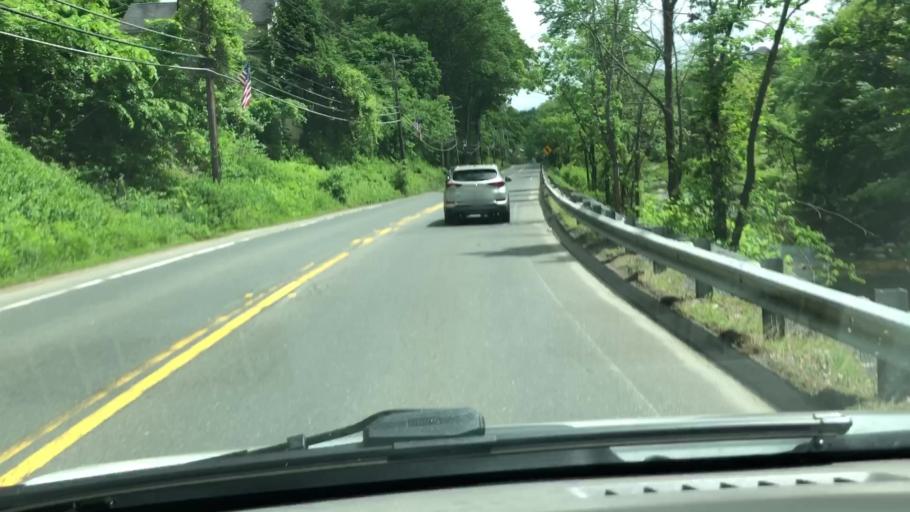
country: US
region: Massachusetts
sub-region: Hampshire County
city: Williamsburg
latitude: 42.3799
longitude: -72.7067
